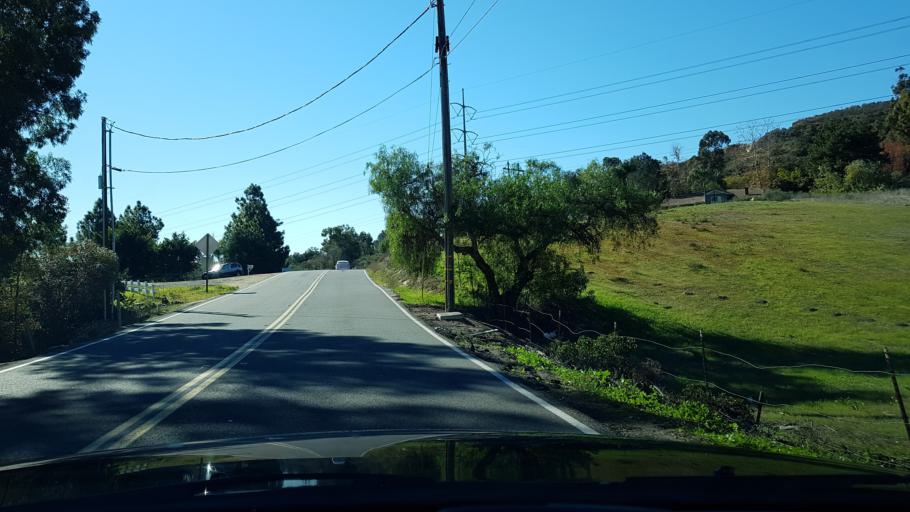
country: US
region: California
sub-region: San Diego County
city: Rancho Santa Fe
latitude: 33.0262
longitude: -117.2451
